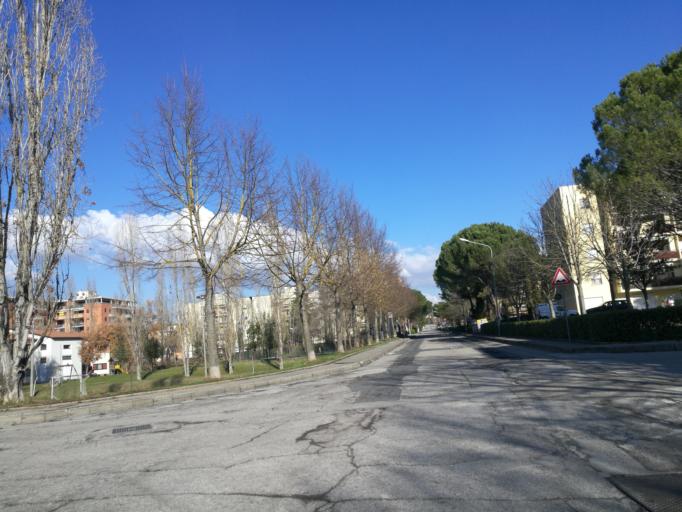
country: IT
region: Umbria
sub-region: Provincia di Perugia
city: Lacugnano
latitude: 43.0780
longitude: 12.3676
